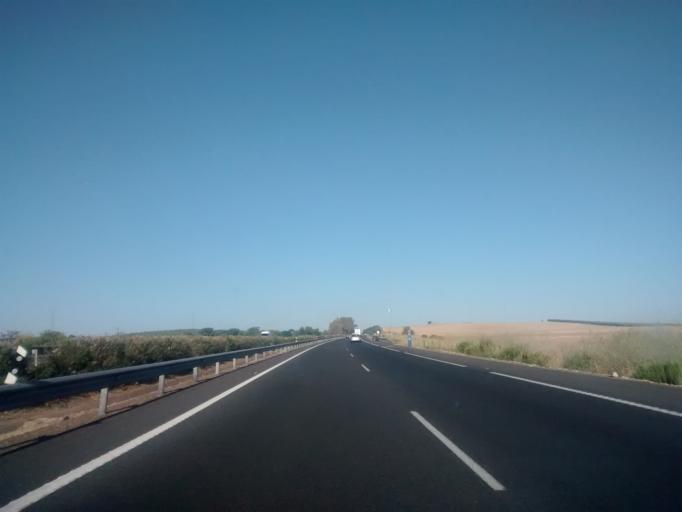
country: ES
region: Andalusia
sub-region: Provincia de Sevilla
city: Carrion de los Cespedes
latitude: 37.3558
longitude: -6.3463
